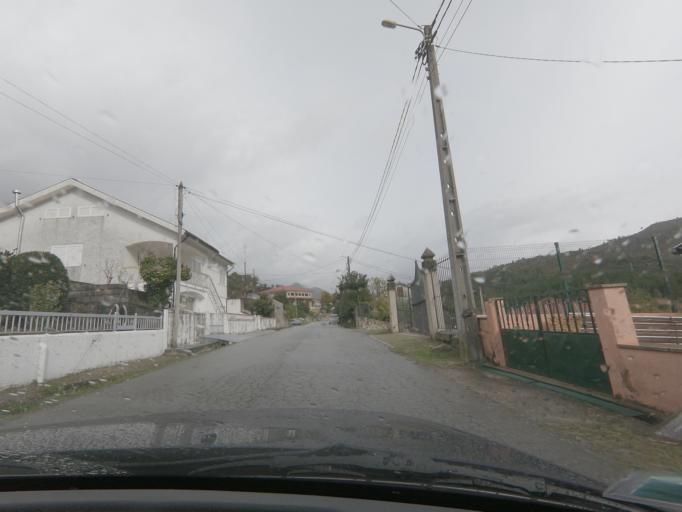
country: PT
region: Vila Real
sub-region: Mondim de Basto
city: Mondim de Basto
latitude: 41.3802
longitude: -7.9462
